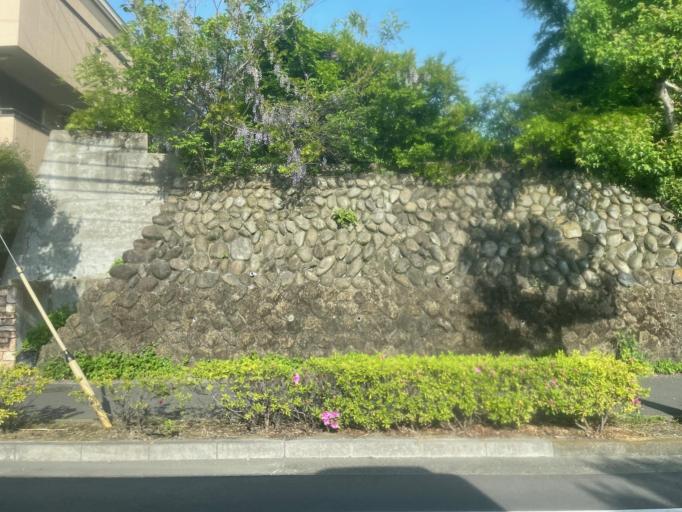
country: JP
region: Tochigi
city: Ashikaga
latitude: 36.3302
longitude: 139.4746
